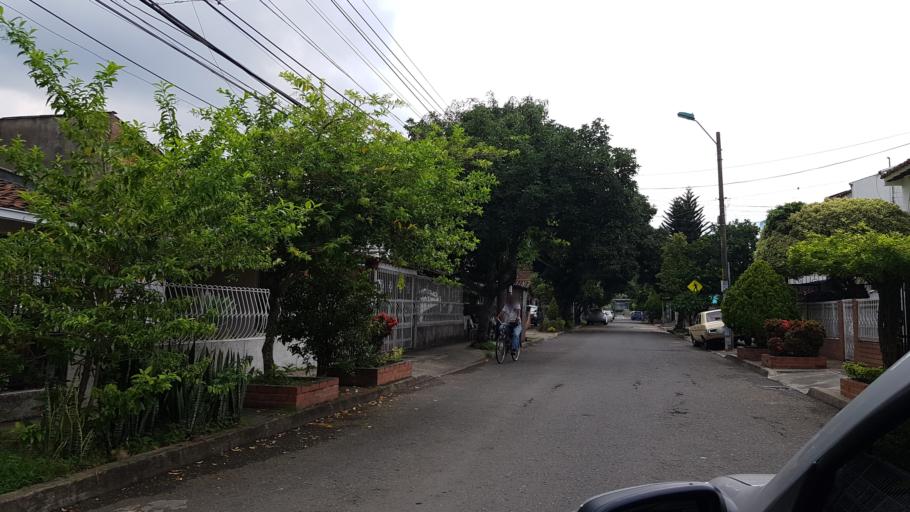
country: CO
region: Valle del Cauca
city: Cali
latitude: 3.3881
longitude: -76.5426
